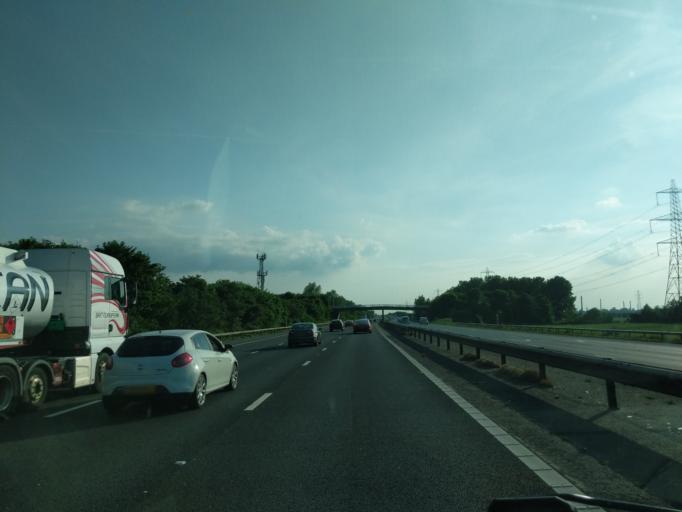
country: GB
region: England
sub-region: Cheshire West and Chester
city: Helsby
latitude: 53.2790
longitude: -2.7706
